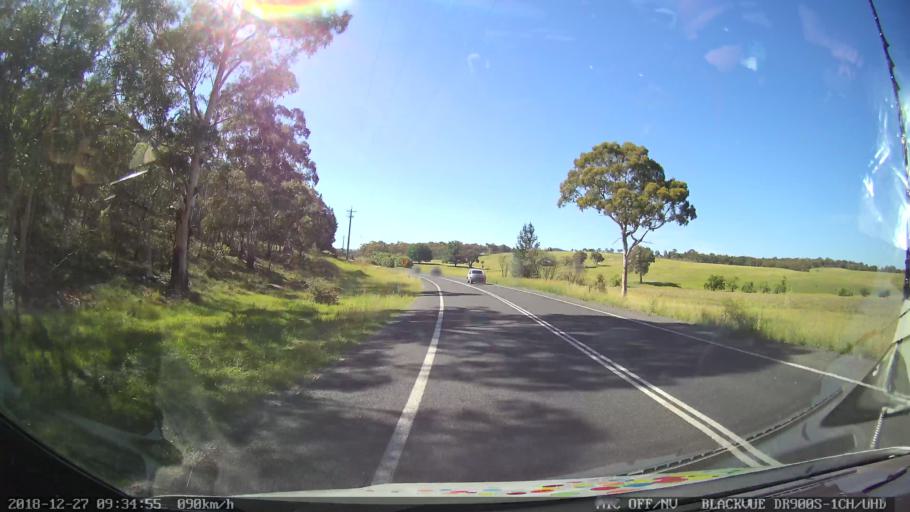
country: AU
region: New South Wales
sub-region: Lithgow
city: Portland
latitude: -33.2324
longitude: 150.0263
